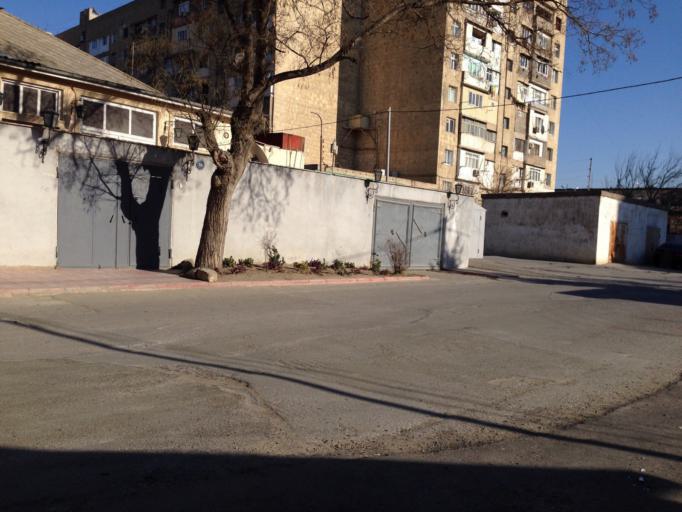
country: AZ
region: Baki
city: Baku
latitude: 40.3920
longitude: 49.8767
